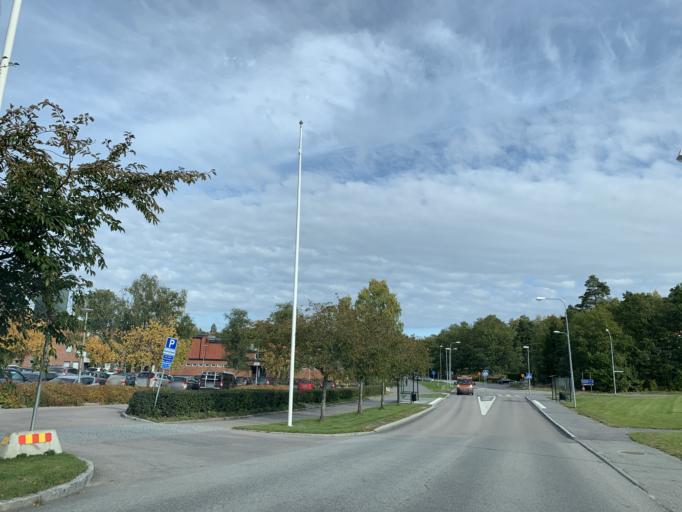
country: SE
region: Soedermanland
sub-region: Eskilstuna Kommun
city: Eskilstuna
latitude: 59.3639
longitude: 16.5394
